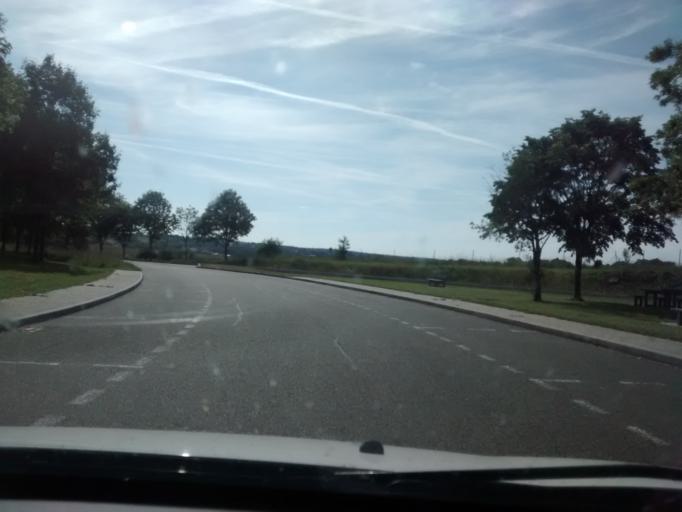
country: FR
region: Pays de la Loire
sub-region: Departement de la Mayenne
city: Loiron
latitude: 48.0765
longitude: -0.9226
